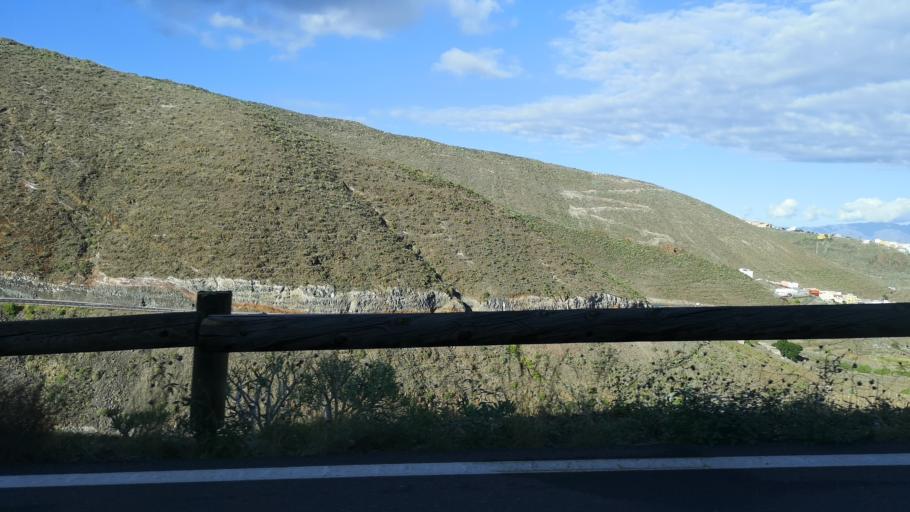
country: ES
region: Canary Islands
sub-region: Provincia de Santa Cruz de Tenerife
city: San Sebastian de la Gomera
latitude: 28.0852
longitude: -17.1266
